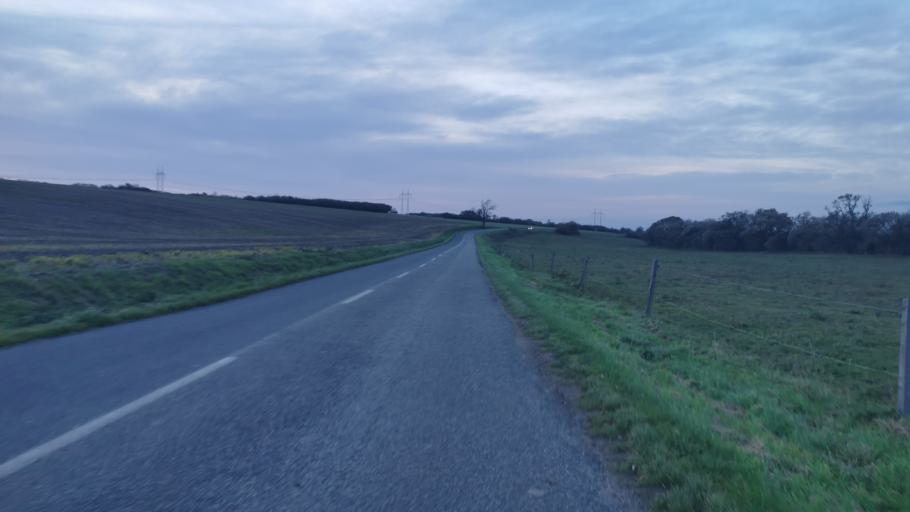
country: CZ
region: South Moravian
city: Sudomerice
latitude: 48.8351
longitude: 17.2797
